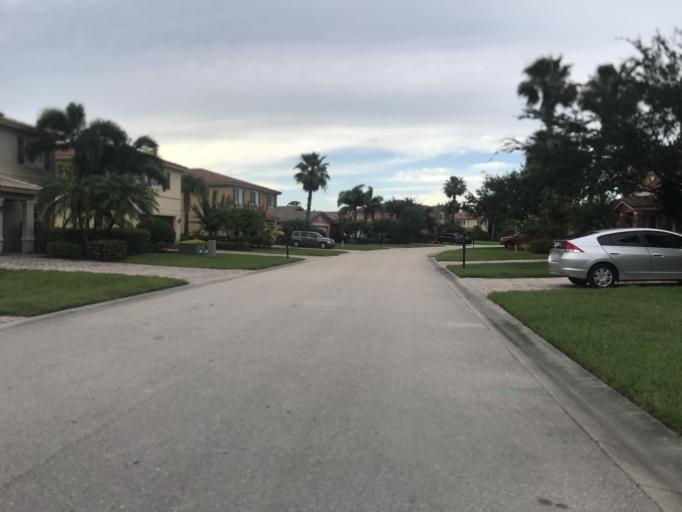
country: US
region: Florida
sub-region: Indian River County
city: Winter Beach
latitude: 27.6951
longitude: -80.4335
